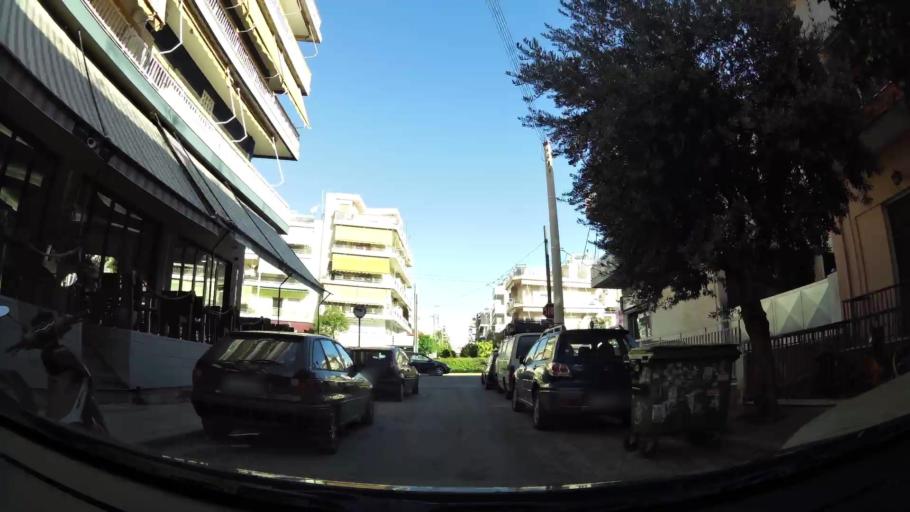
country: GR
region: Attica
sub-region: Nomos Piraios
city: Agios Ioannis Rentis
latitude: 37.9728
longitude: 23.6605
